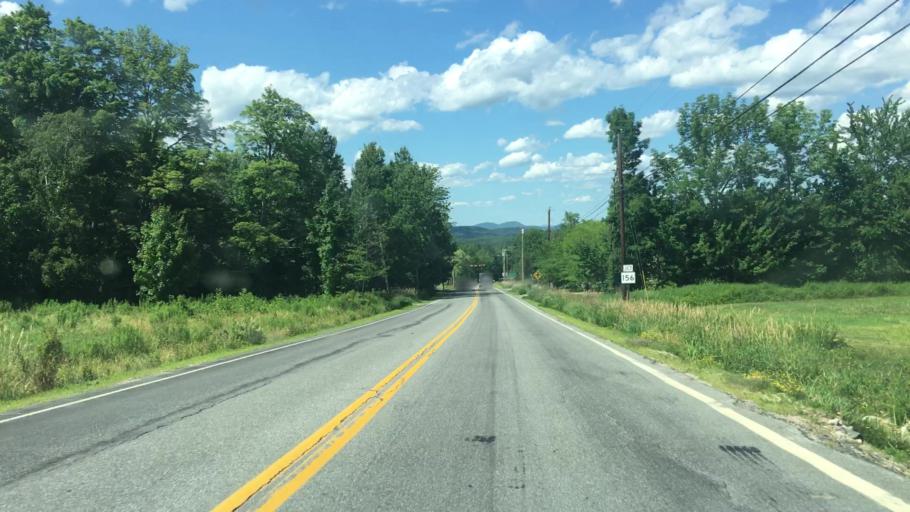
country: US
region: Maine
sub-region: Franklin County
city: Wilton
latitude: 44.5749
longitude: -70.1756
